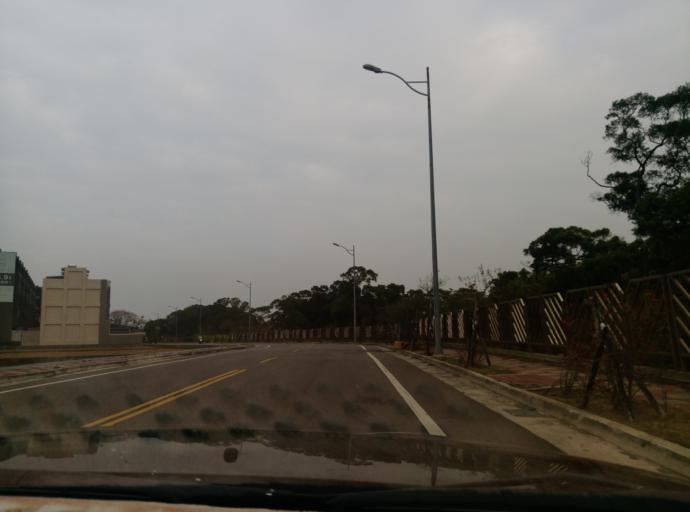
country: TW
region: Taiwan
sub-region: Hsinchu
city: Hsinchu
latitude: 24.7030
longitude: 120.9041
